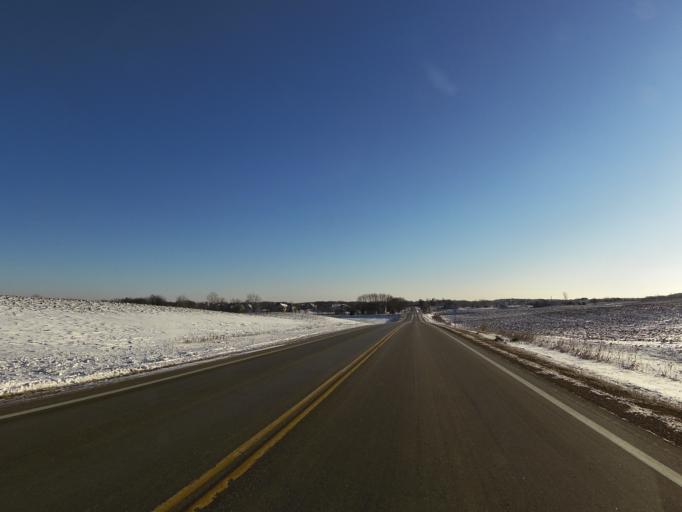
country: US
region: Minnesota
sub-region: Scott County
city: Shakopee
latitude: 44.7327
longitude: -93.5463
